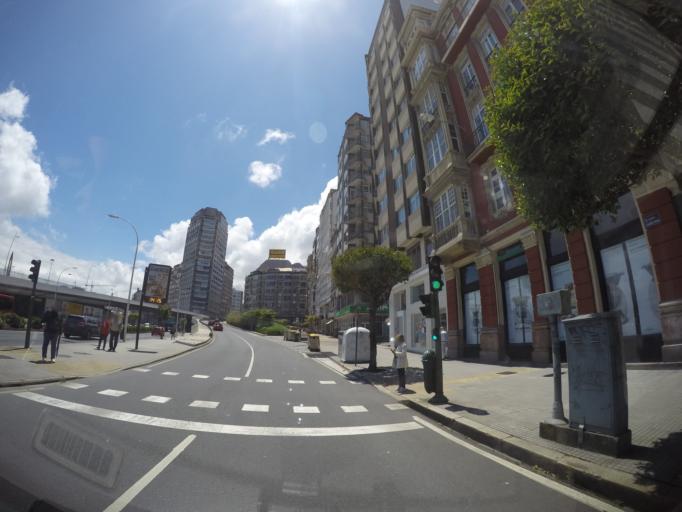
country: ES
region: Galicia
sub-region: Provincia da Coruna
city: A Coruna
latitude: 43.3622
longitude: -8.4054
